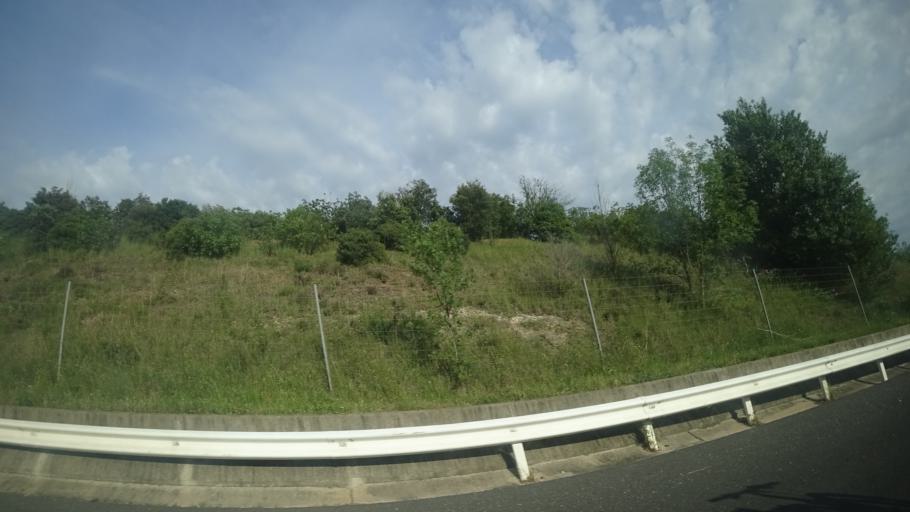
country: FR
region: Languedoc-Roussillon
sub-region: Departement de l'Herault
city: Nebian
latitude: 43.6460
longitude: 3.4493
